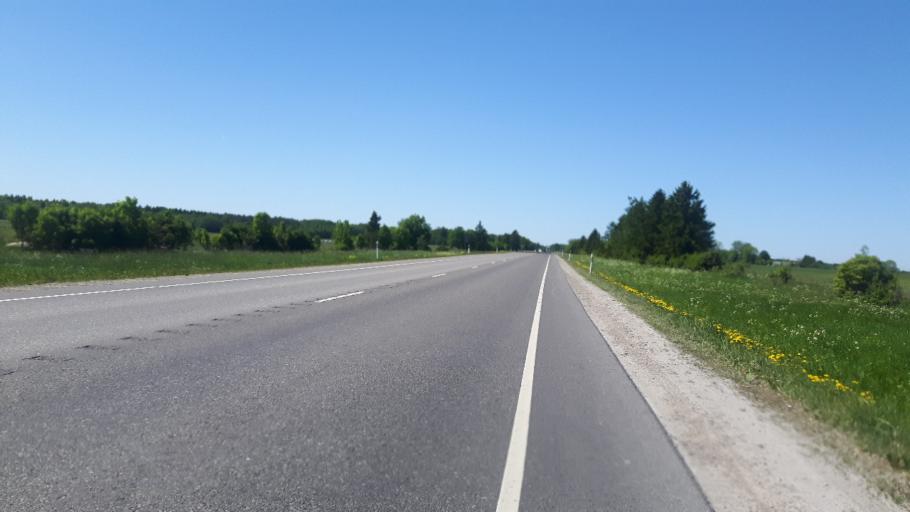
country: EE
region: Ida-Virumaa
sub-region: Sillamaee linn
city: Sillamae
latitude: 59.3921
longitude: 27.6825
